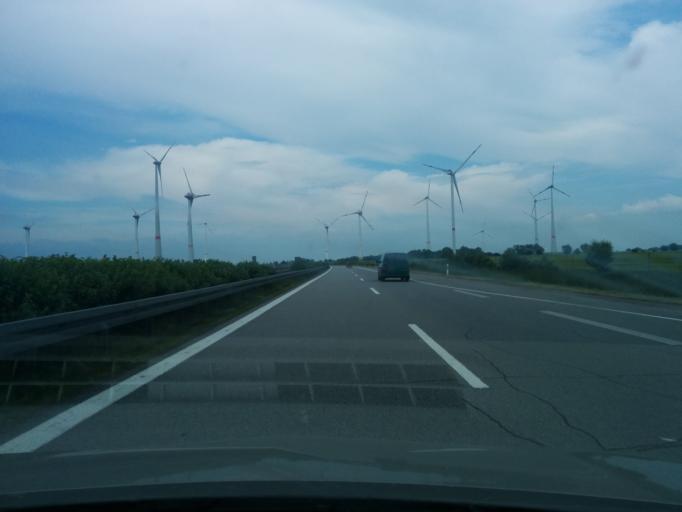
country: DE
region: Mecklenburg-Vorpommern
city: Kessin
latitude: 53.7128
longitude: 13.3310
